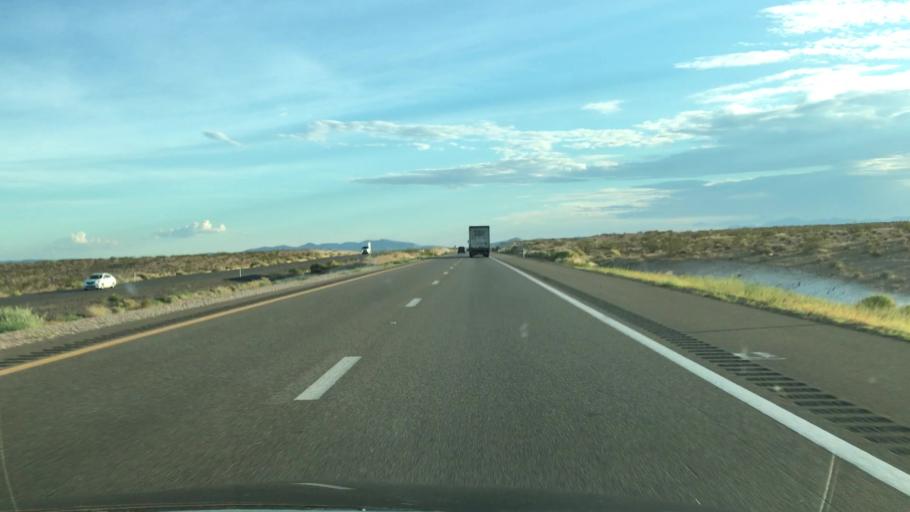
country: US
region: Nevada
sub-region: Clark County
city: Moapa Town
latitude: 36.5258
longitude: -114.7312
